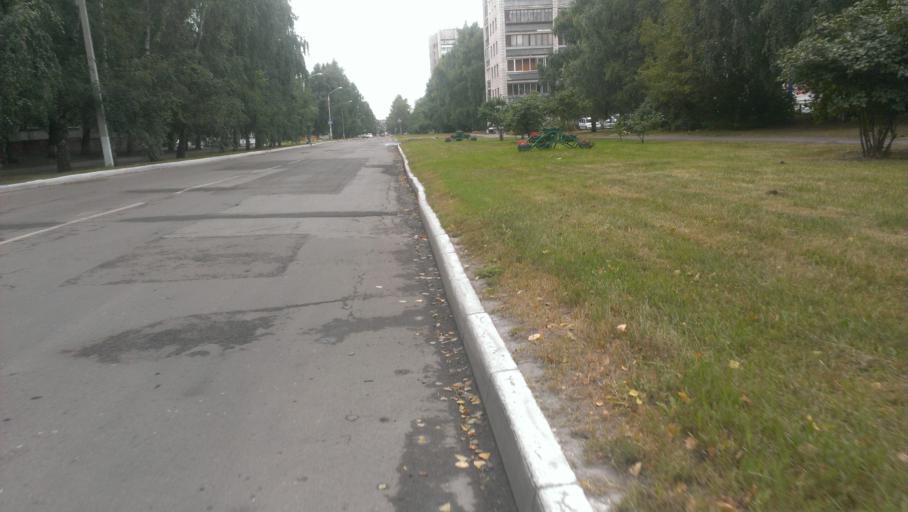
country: RU
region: Altai Krai
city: Novosilikatnyy
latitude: 53.3722
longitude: 83.6698
